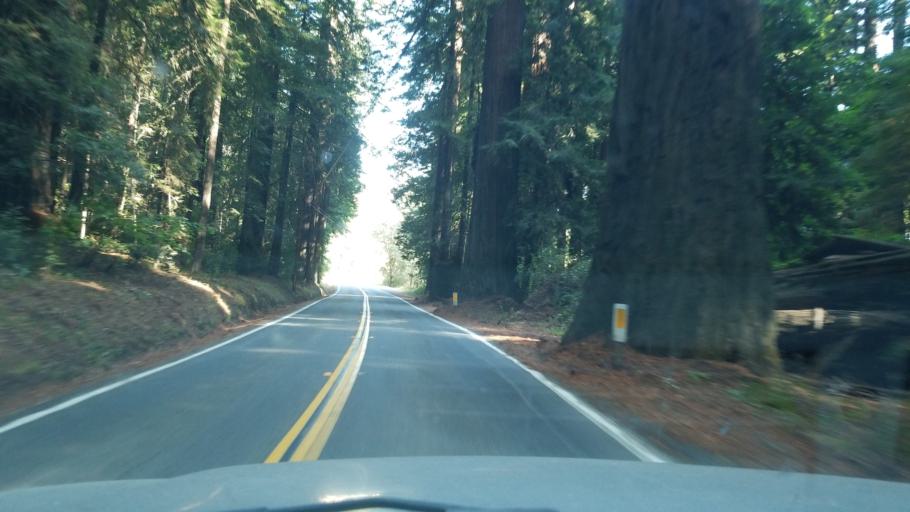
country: US
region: California
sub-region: Humboldt County
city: Redway
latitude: 40.2226
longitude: -123.8005
